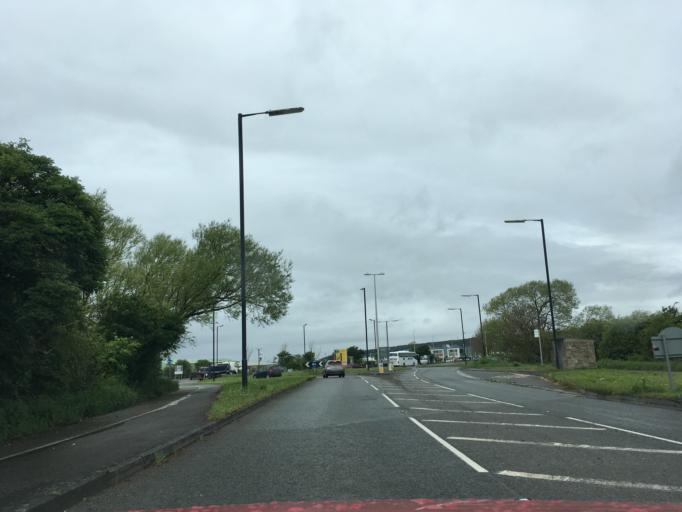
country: GB
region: England
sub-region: North Somerset
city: Hutton
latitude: 51.3389
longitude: -2.9269
